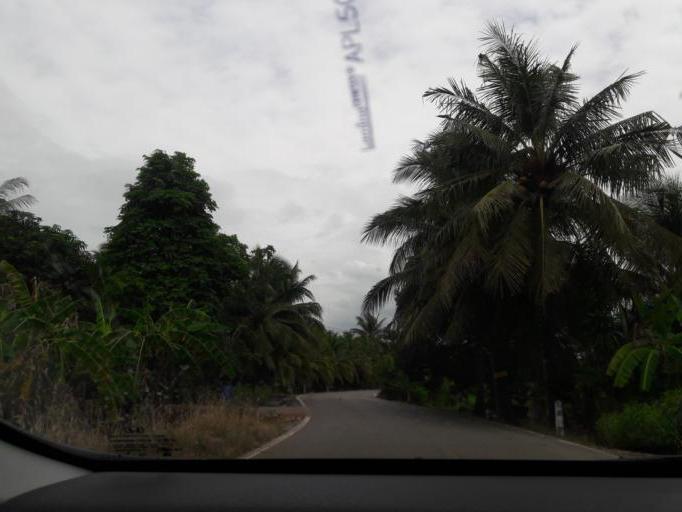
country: TH
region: Ratchaburi
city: Damnoen Saduak
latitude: 13.5647
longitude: 99.9783
